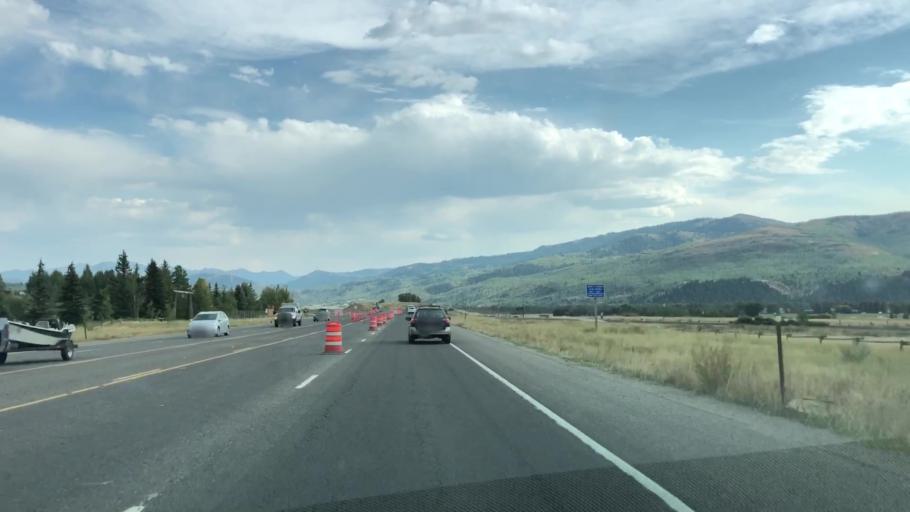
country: US
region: Wyoming
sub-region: Teton County
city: South Park
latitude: 43.4160
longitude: -110.7737
